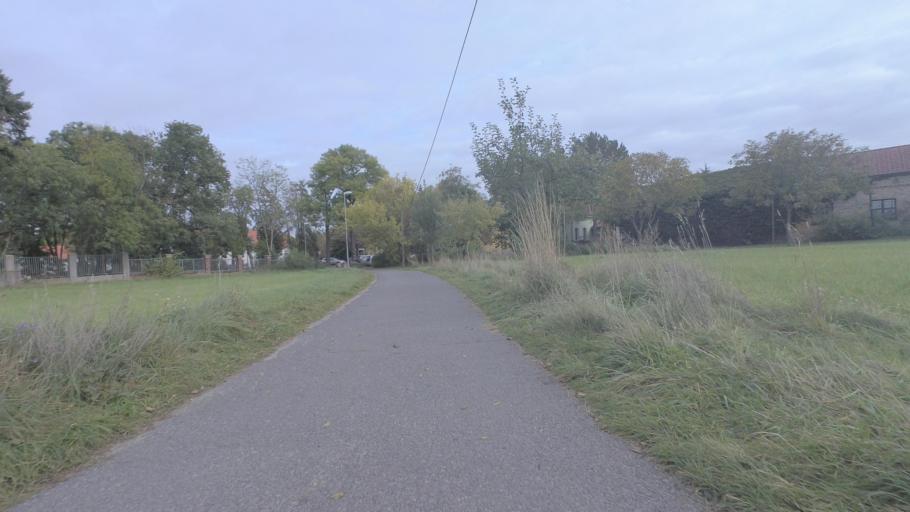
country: DE
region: Brandenburg
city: Grossbeeren
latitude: 52.3132
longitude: 13.3150
